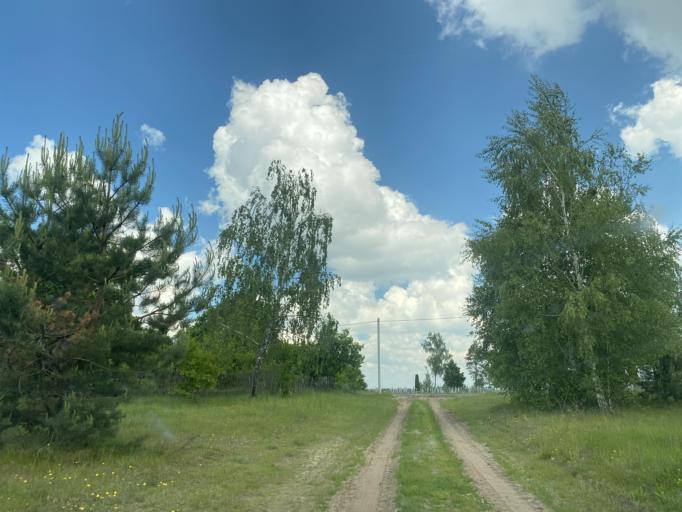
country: BY
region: Brest
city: Ivanava
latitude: 52.2034
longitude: 25.6079
